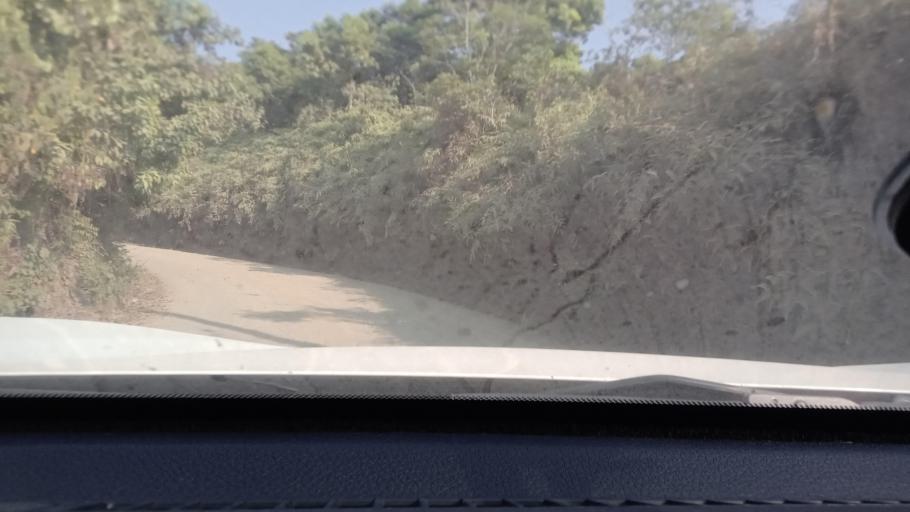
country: MX
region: Tabasco
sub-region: Huimanguillo
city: Francisco Rueda
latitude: 17.6530
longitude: -93.8830
